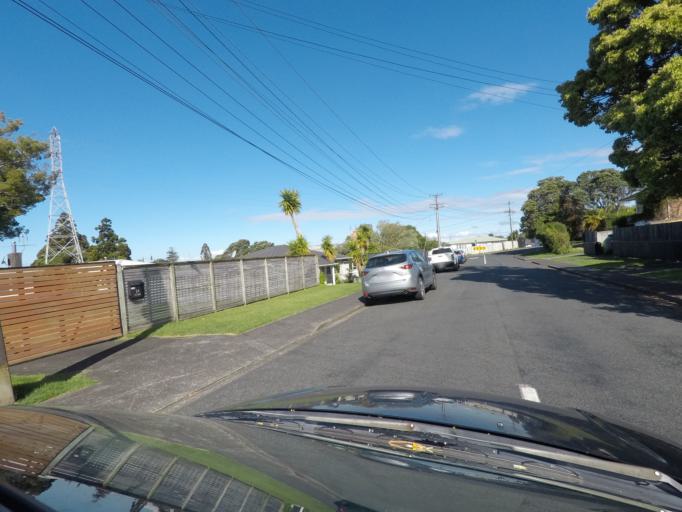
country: NZ
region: Auckland
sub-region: Auckland
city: Rosebank
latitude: -36.8675
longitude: 174.6496
